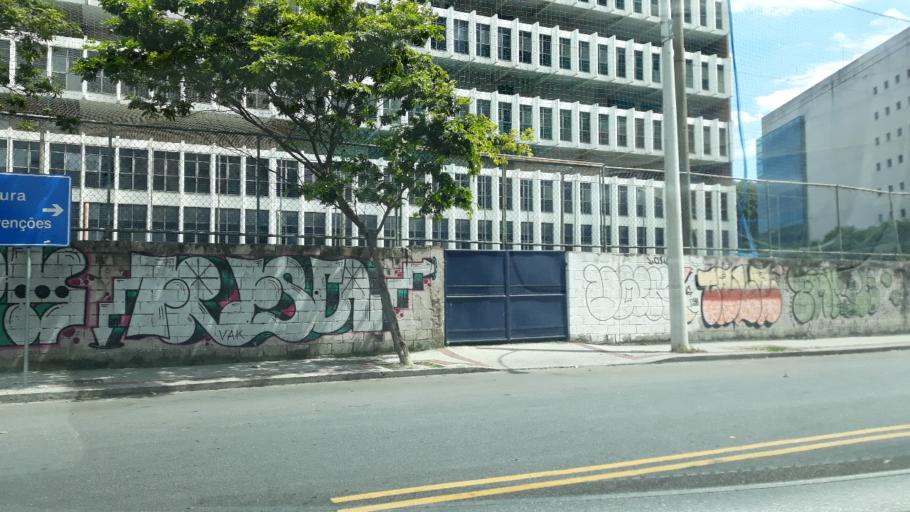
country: BR
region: Rio de Janeiro
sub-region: Rio De Janeiro
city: Rio de Janeiro
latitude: -22.9105
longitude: -43.2020
